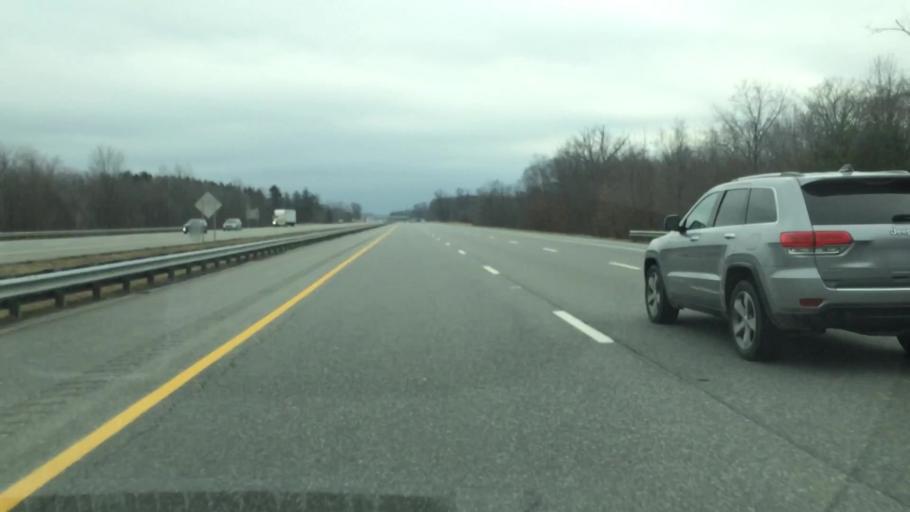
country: US
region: Ohio
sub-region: Cuyahoga County
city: Strongsville
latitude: 41.2877
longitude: -81.8067
